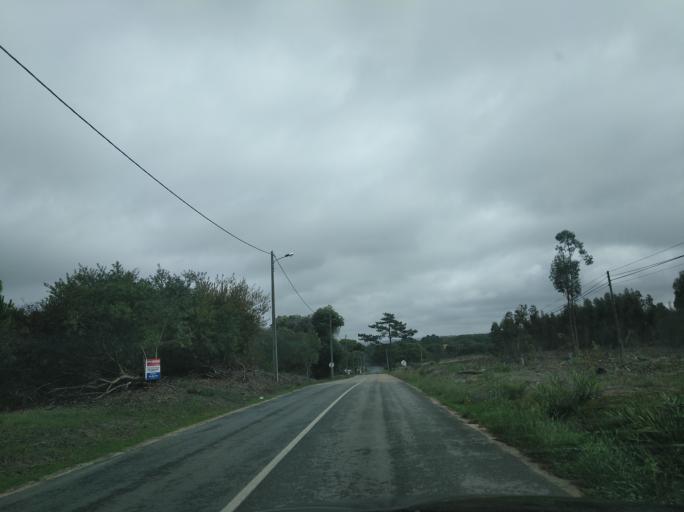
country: PT
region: Setubal
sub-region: Santiago do Cacem
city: Santo Andre
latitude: 38.1312
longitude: -8.7803
